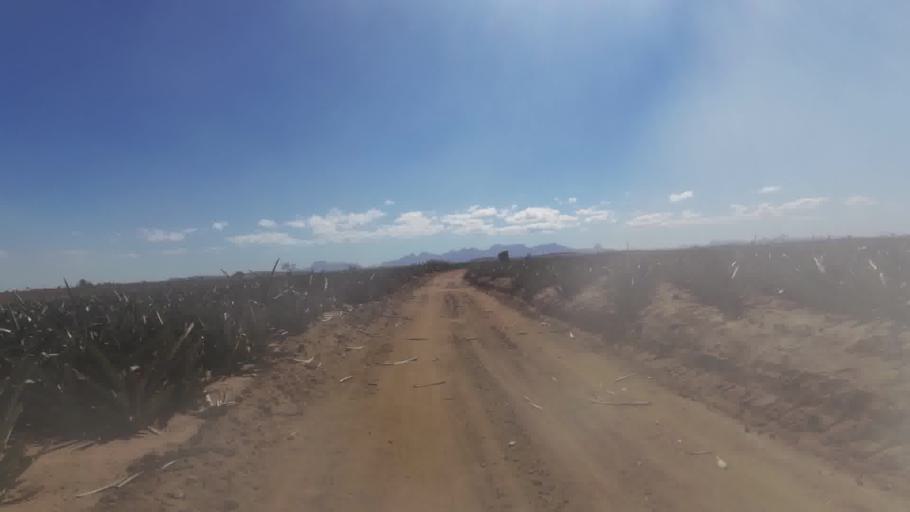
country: BR
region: Espirito Santo
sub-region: Marataizes
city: Marataizes
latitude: -21.1544
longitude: -40.9568
